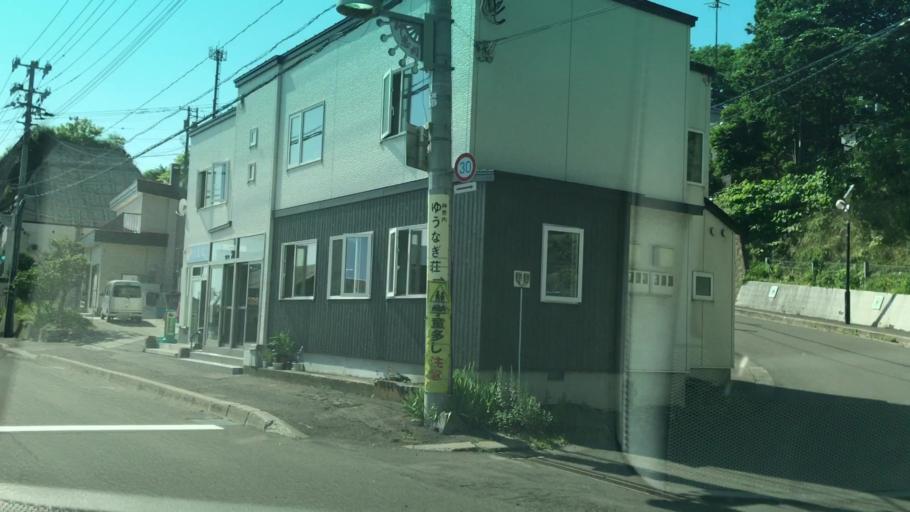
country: JP
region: Hokkaido
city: Iwanai
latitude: 43.1434
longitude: 140.4276
